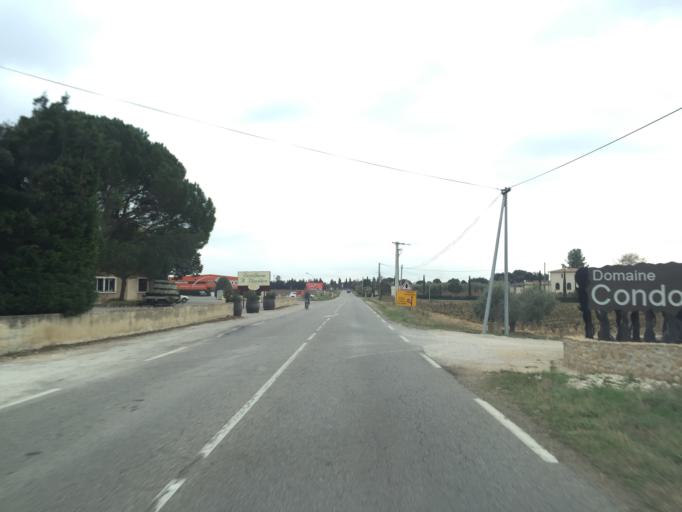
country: FR
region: Provence-Alpes-Cote d'Azur
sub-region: Departement du Vaucluse
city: Chateauneuf-du-Pape
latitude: 44.0394
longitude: 4.8531
